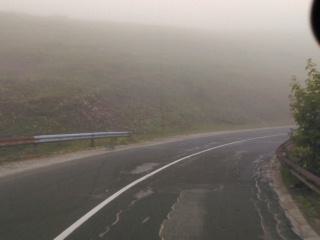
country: BG
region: Lovech
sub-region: Obshtina Troyan
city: Troyan
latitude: 42.7774
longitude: 24.6091
